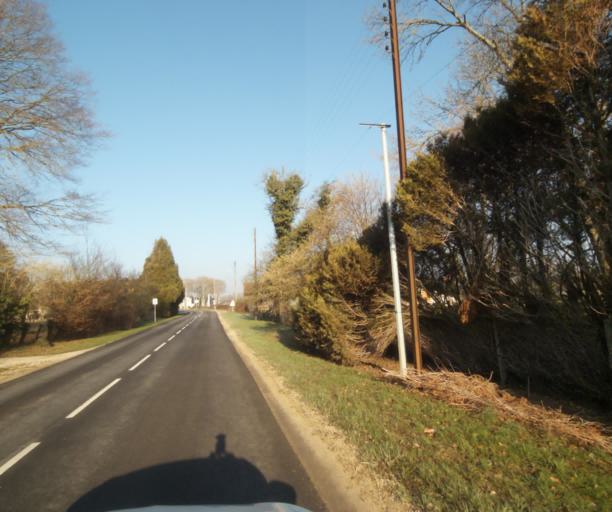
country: FR
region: Champagne-Ardenne
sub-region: Departement de la Haute-Marne
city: Montier-en-Der
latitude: 48.4632
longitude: 4.7658
